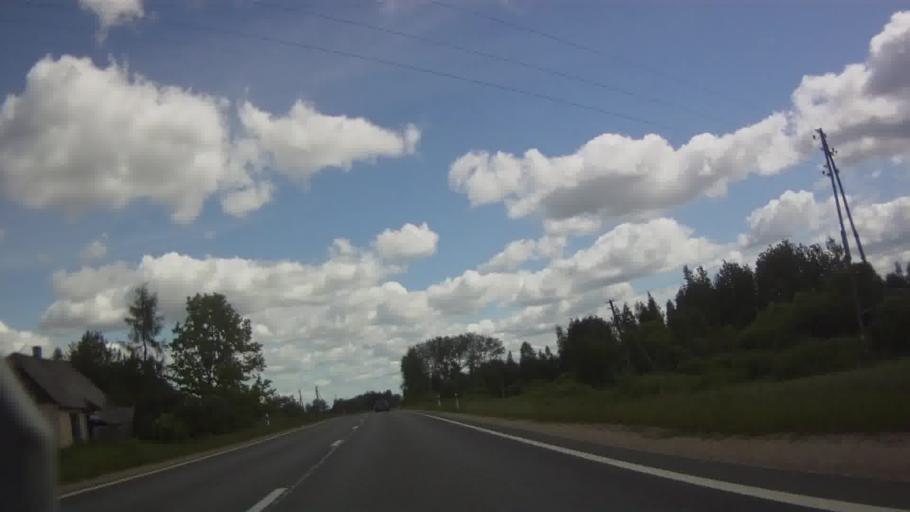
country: LV
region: Livani
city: Livani
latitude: 56.5301
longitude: 26.2240
